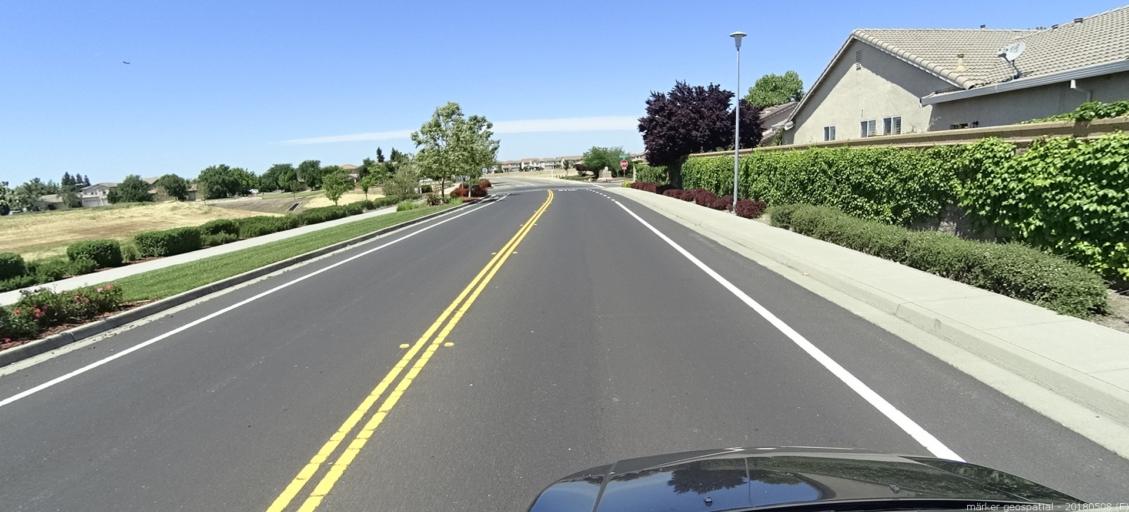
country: US
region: California
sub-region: Sacramento County
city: Elverta
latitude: 38.6664
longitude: -121.5233
